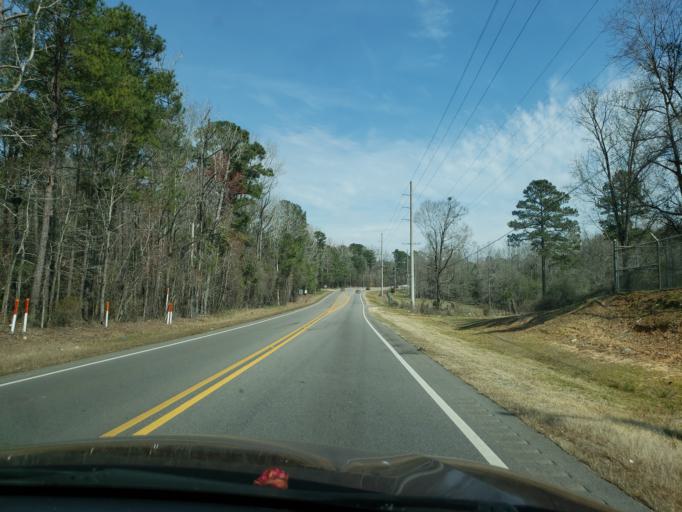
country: US
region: Alabama
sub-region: Elmore County
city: Wetumpka
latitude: 32.5546
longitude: -86.1579
